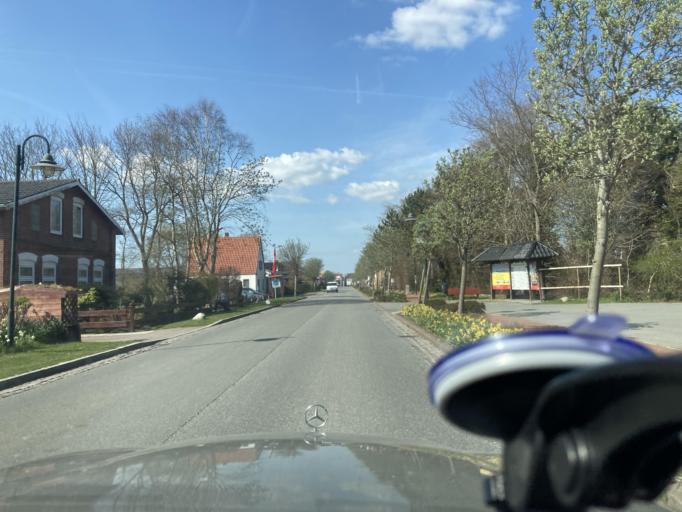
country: DE
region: Schleswig-Holstein
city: Krempel
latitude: 54.3237
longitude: 9.0255
